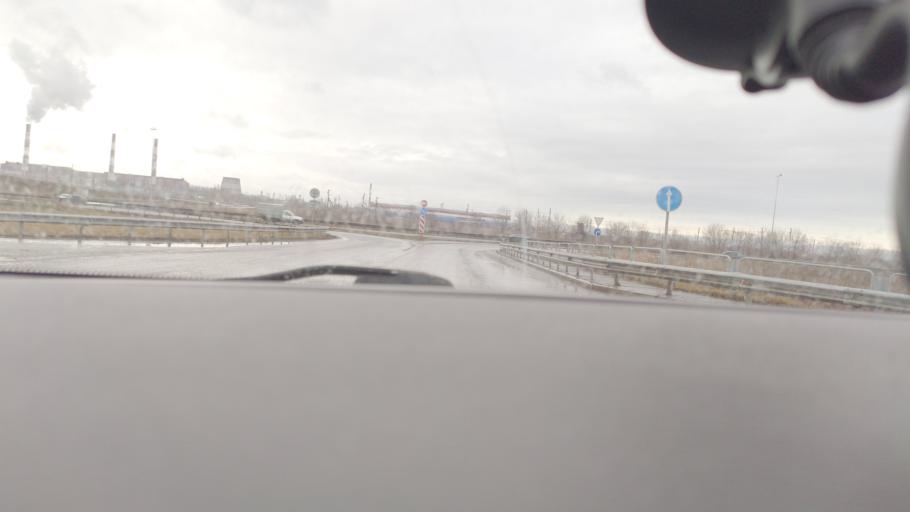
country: RU
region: Perm
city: Kondratovo
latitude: 57.9385
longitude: 56.1591
